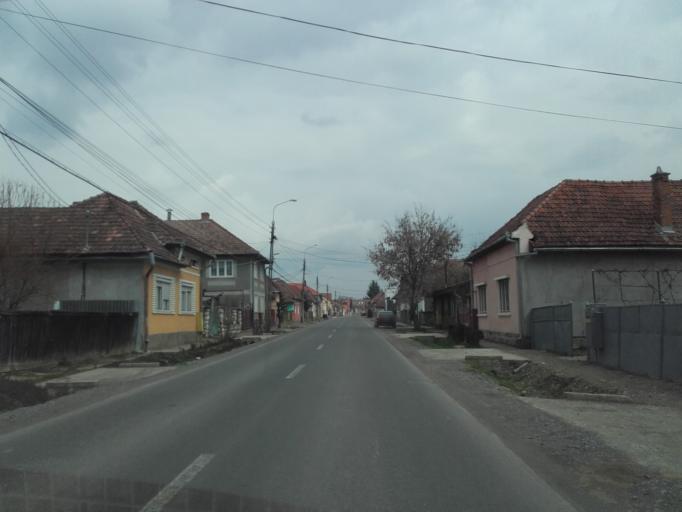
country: RO
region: Mures
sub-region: Comuna Miercurea Nirajului
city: Miercurea Nirajului
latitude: 46.5323
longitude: 24.7911
